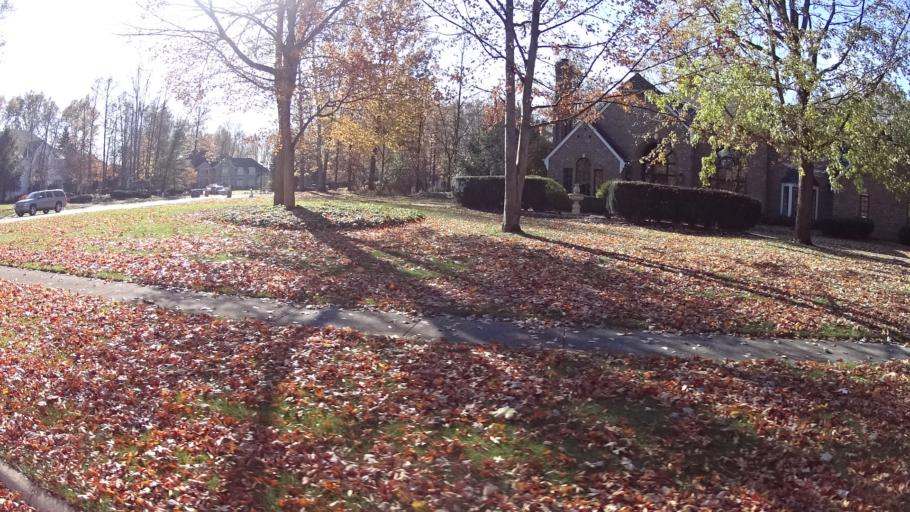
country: US
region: Ohio
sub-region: Lorain County
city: Avon Lake
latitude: 41.4959
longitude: -82.0031
